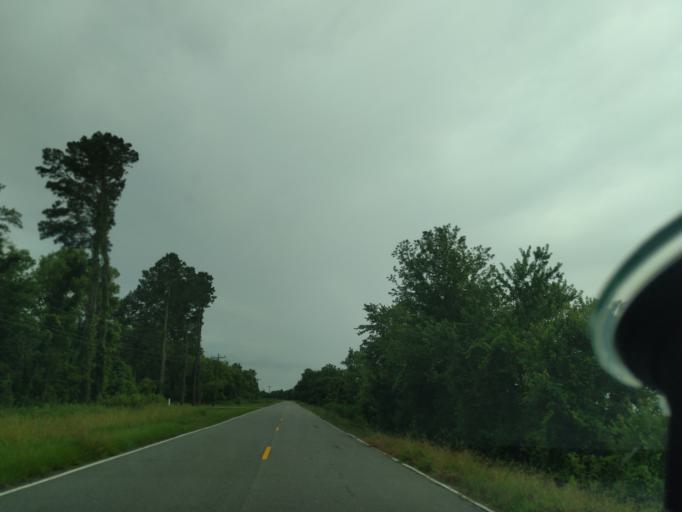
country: US
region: North Carolina
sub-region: Washington County
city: Plymouth
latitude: 35.7835
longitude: -76.5217
